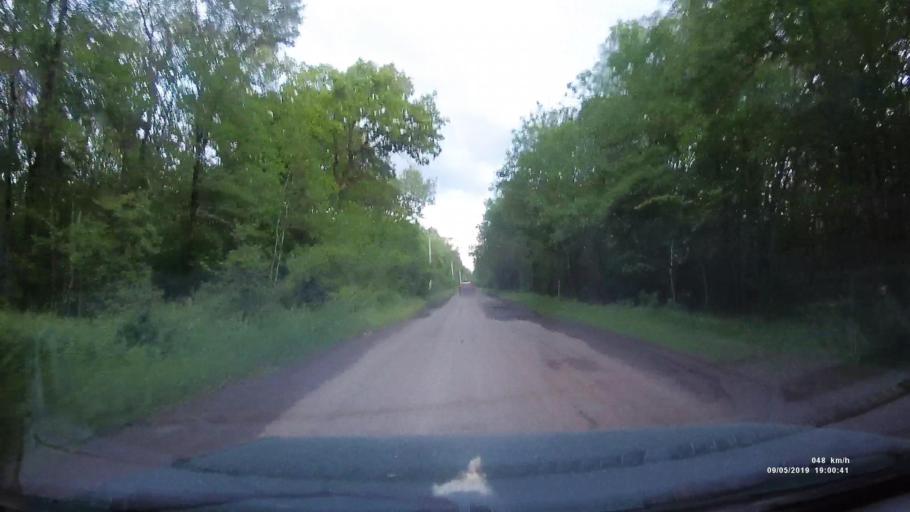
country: RU
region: Krasnodarskiy
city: Kanelovskaya
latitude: 46.7509
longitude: 39.1381
